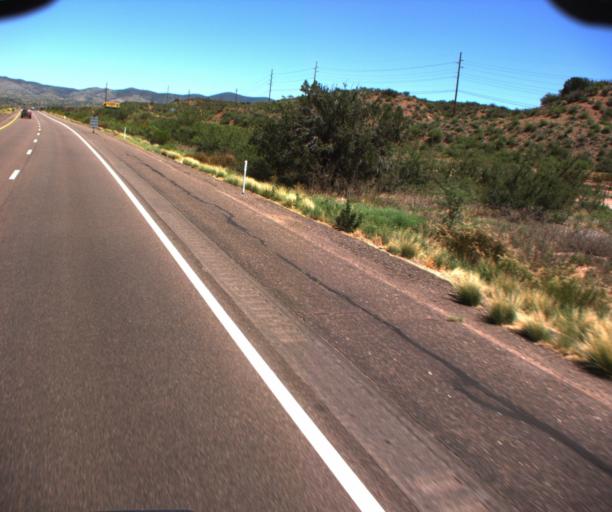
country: US
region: Arizona
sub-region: Gila County
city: Payson
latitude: 34.0911
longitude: -111.3534
